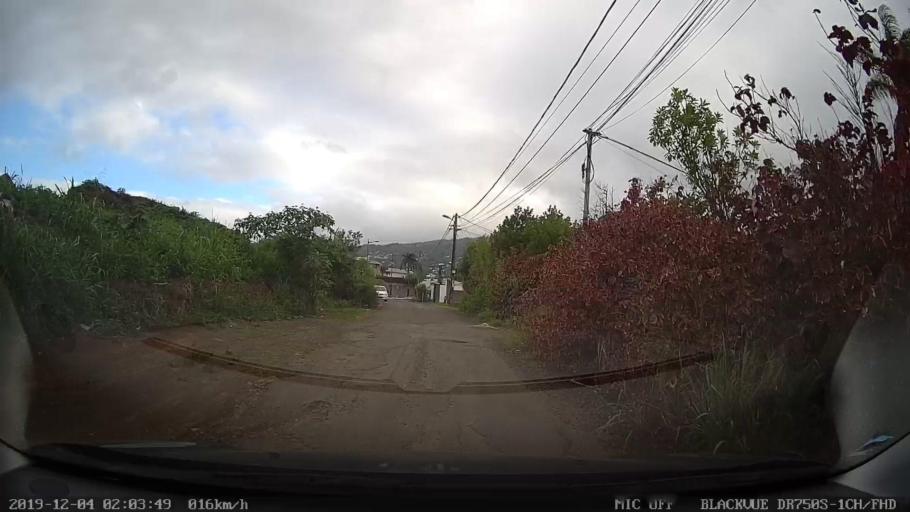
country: RE
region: Reunion
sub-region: Reunion
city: Sainte-Marie
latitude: -20.9219
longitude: 55.5254
